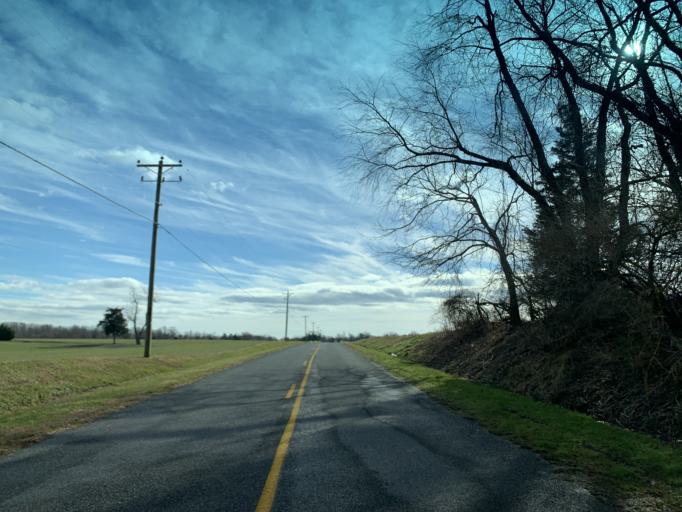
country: US
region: Maryland
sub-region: Kent County
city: Chestertown
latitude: 39.3363
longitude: -76.0473
